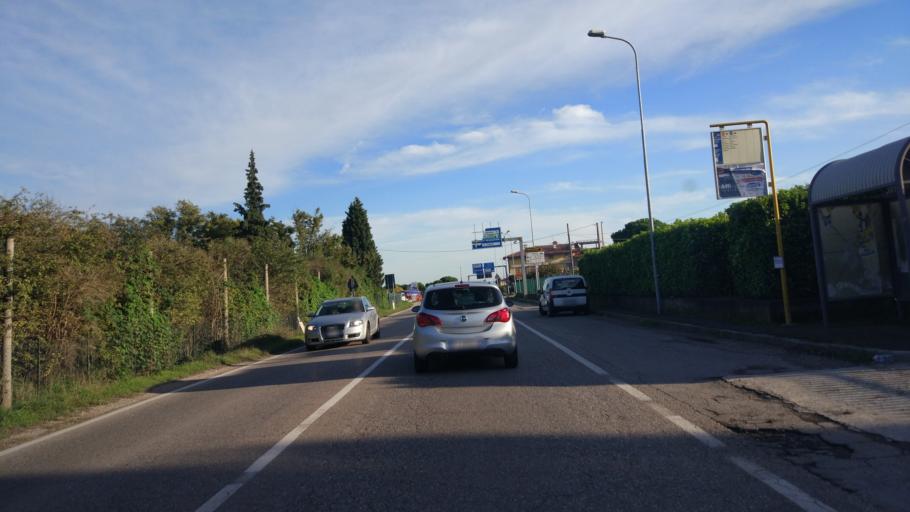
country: IT
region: Veneto
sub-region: Provincia di Verona
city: Ospedaletto
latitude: 45.5006
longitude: 10.8590
